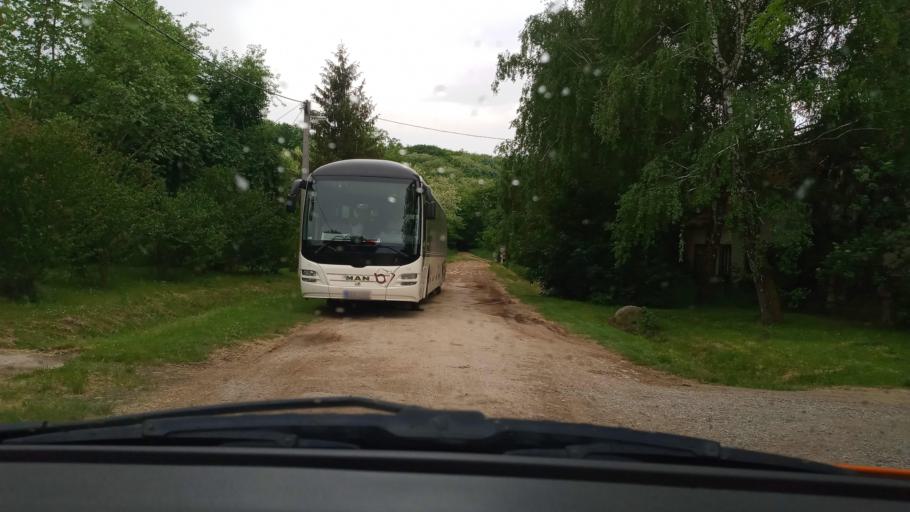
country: HU
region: Baranya
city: Harkany
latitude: 45.8961
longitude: 18.1363
